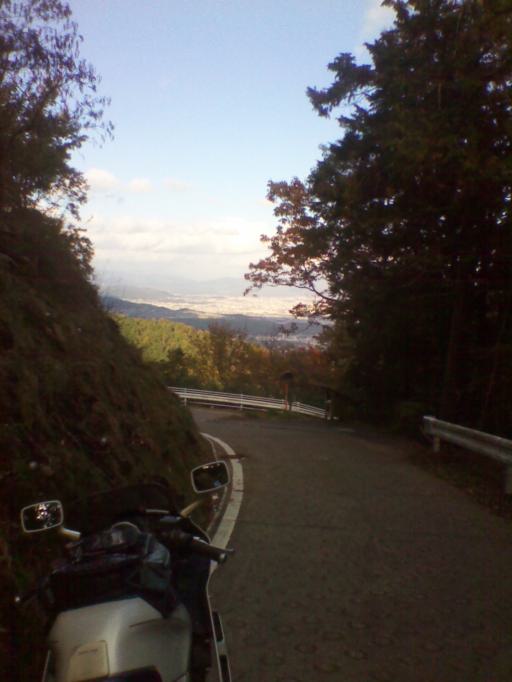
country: JP
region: Kyoto
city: Muko
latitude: 34.9508
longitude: 135.6403
